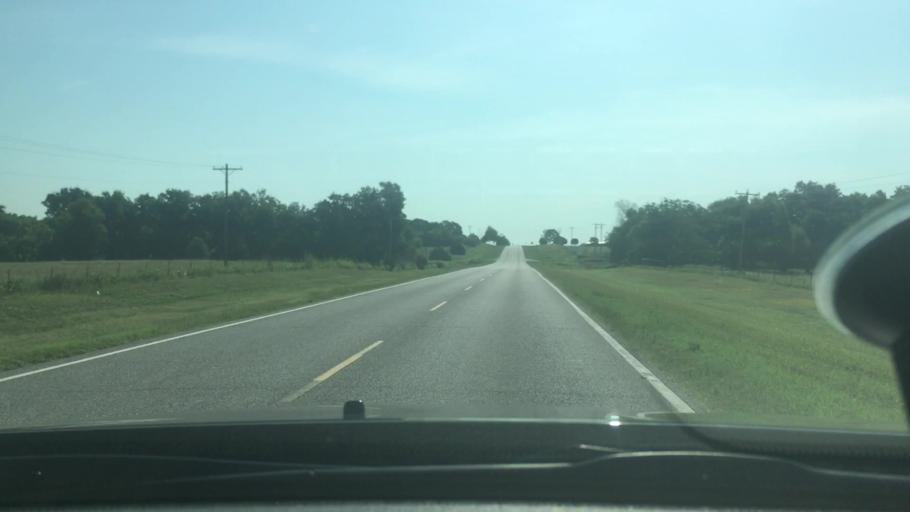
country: US
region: Oklahoma
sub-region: Garvin County
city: Wynnewood
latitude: 34.6517
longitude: -97.2327
